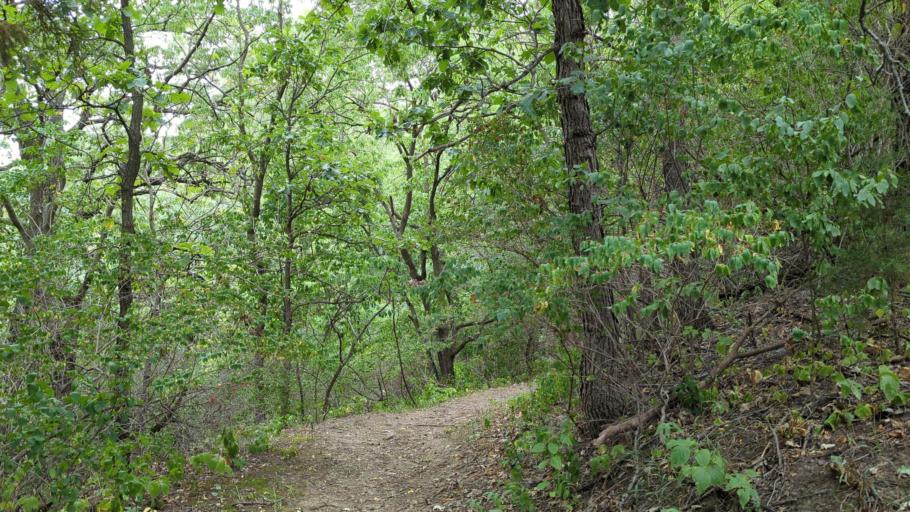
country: US
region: South Dakota
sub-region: Union County
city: Beresford
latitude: 42.9233
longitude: -96.7795
